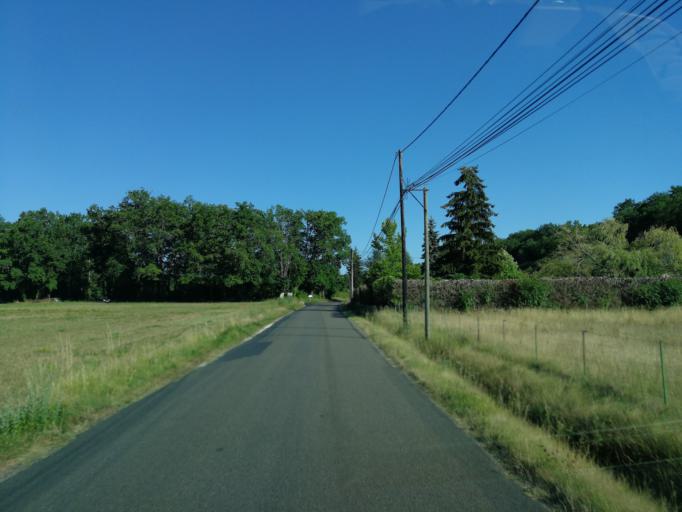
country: FR
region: Midi-Pyrenees
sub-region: Departement du Lot
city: Gourdon
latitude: 44.7608
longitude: 1.3738
